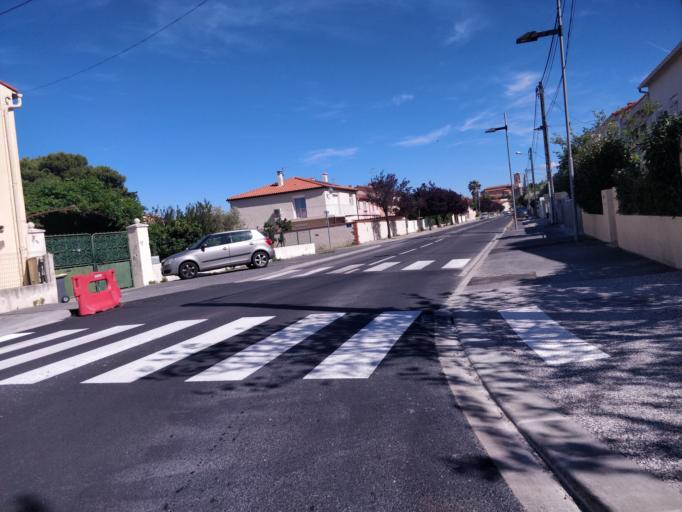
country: FR
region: Languedoc-Roussillon
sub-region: Departement des Pyrenees-Orientales
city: Elne
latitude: 42.6049
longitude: 2.9665
